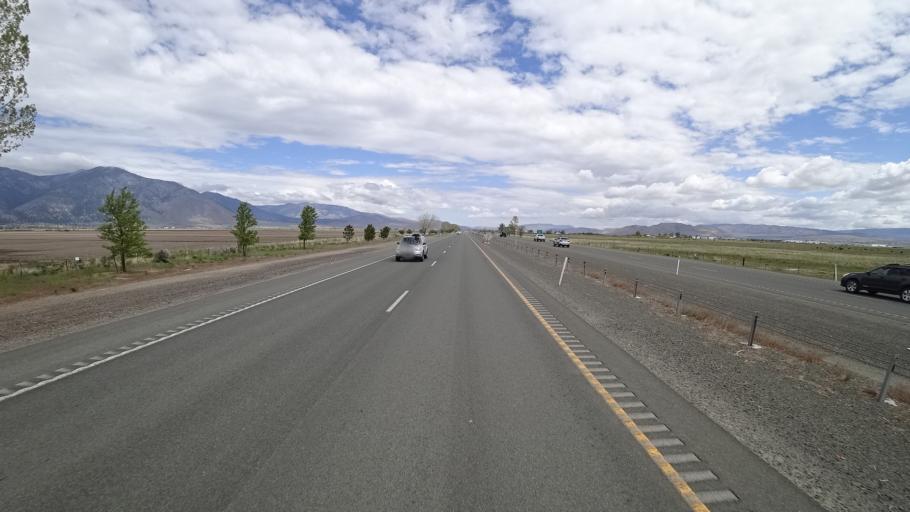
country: US
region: Nevada
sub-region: Douglas County
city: Minden
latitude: 38.9851
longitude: -119.7796
